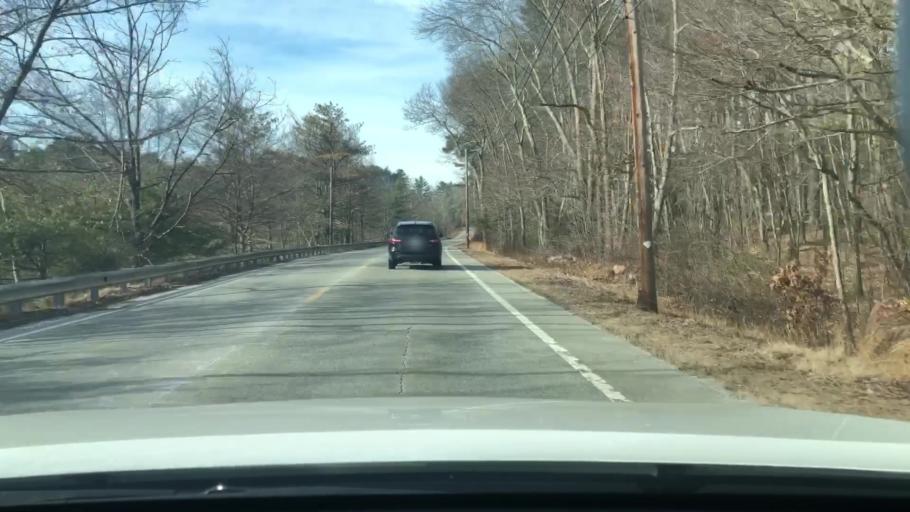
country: US
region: Massachusetts
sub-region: Worcester County
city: Northbridge
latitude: 42.1811
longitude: -71.6428
